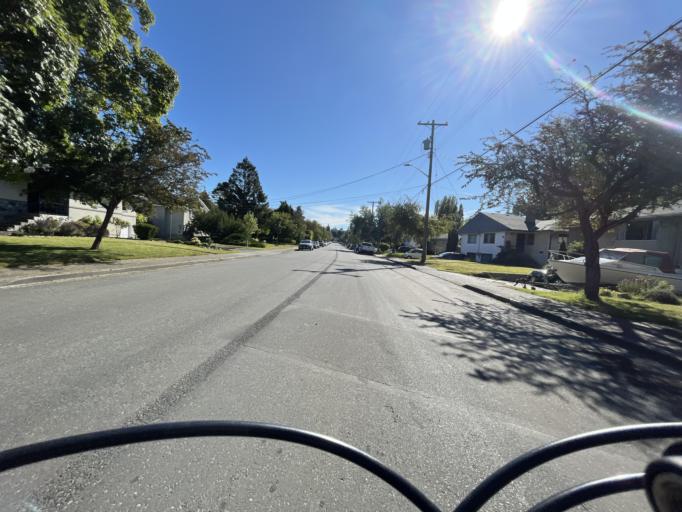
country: CA
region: British Columbia
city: Victoria
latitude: 48.4164
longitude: -123.3355
